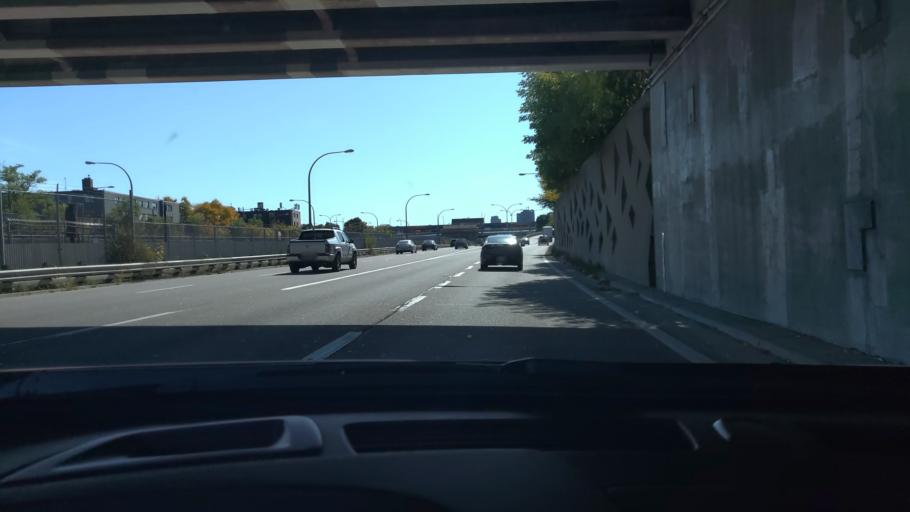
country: CA
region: Ontario
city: Toronto
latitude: 43.7192
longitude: -79.4458
